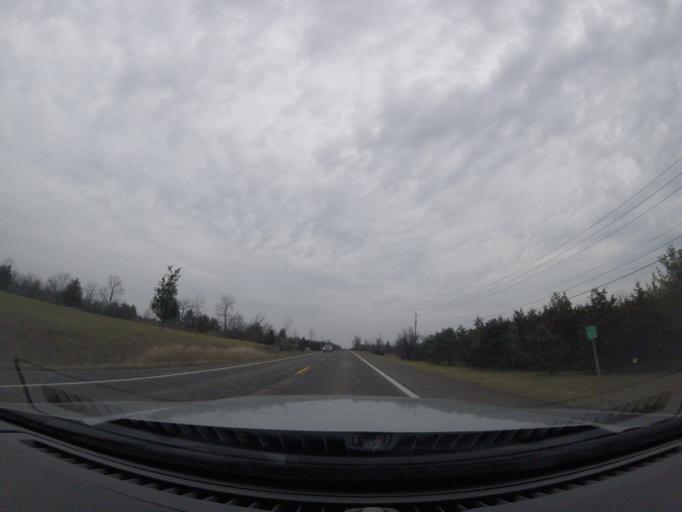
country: US
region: New York
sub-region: Yates County
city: Dundee
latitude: 42.5396
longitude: -76.9183
